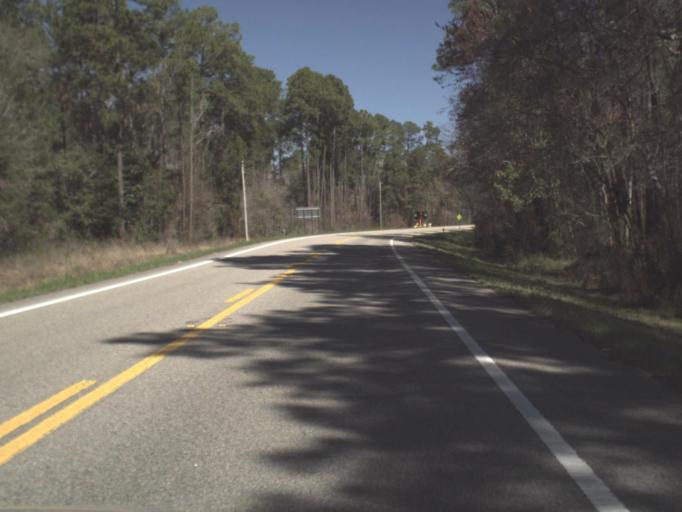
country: US
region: Florida
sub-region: Calhoun County
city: Blountstown
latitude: 30.5453
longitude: -85.0263
